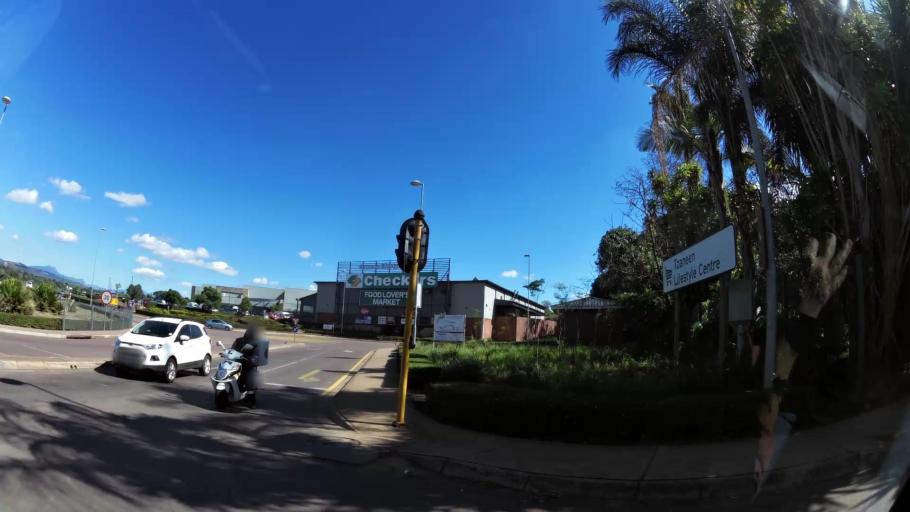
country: ZA
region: Limpopo
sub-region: Mopani District Municipality
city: Tzaneen
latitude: -23.8219
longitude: 30.1586
